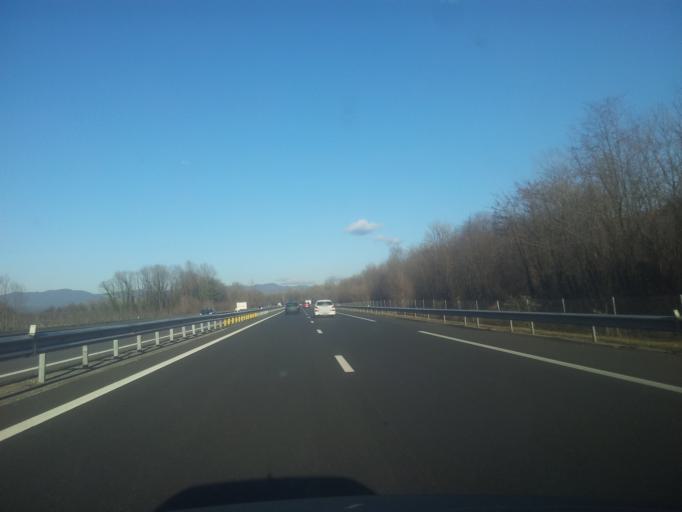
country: FR
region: Rhone-Alpes
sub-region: Departement de l'Isere
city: Saint-Quentin-sur-Isere
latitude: 45.2597
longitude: 5.5132
